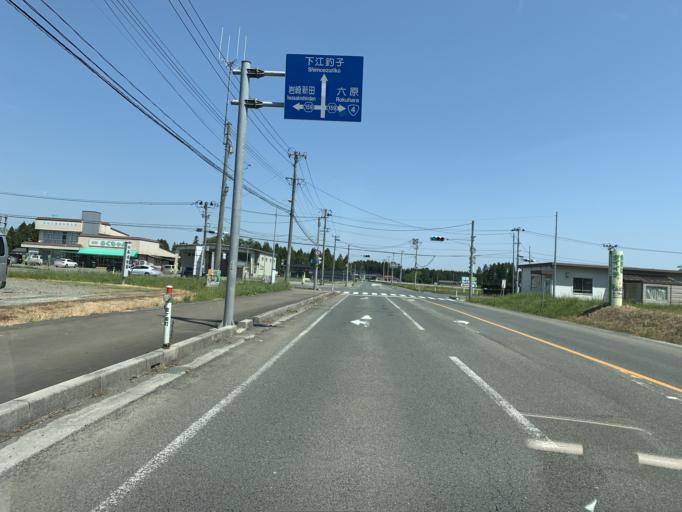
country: JP
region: Iwate
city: Kitakami
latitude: 39.2323
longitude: 141.0667
